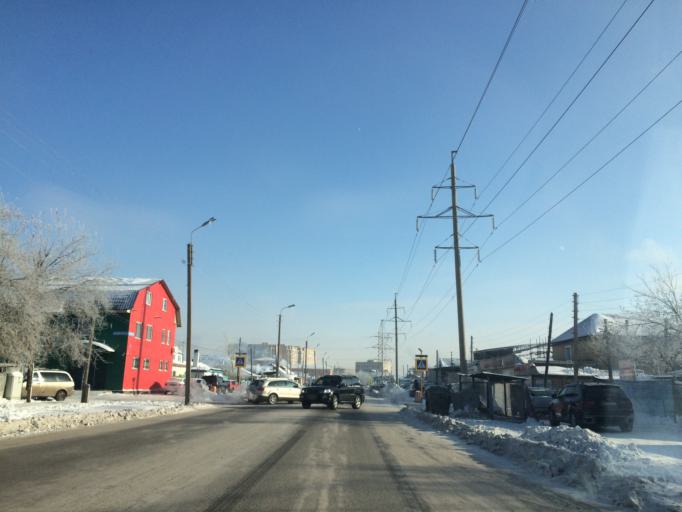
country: KZ
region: Astana Qalasy
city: Astana
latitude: 51.1733
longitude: 71.4422
